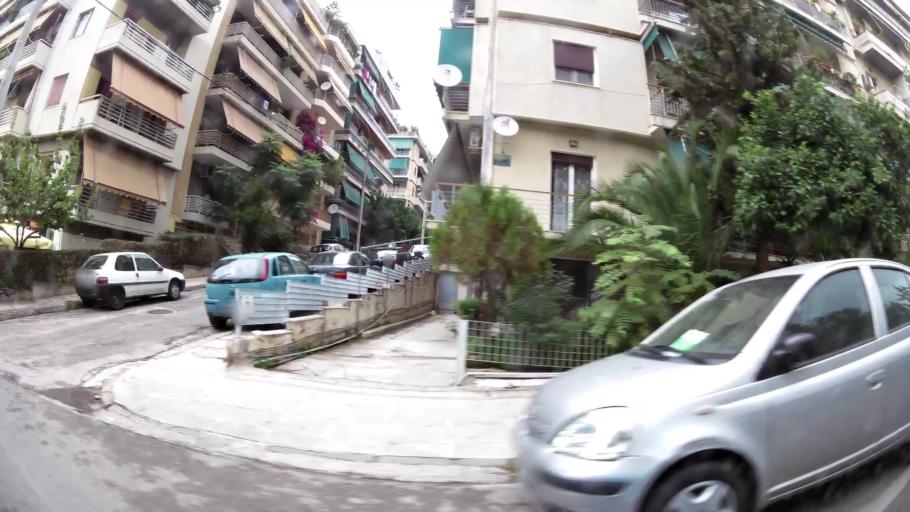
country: GR
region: Attica
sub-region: Nomarchia Athinas
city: Vyronas
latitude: 37.9612
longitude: 23.7561
